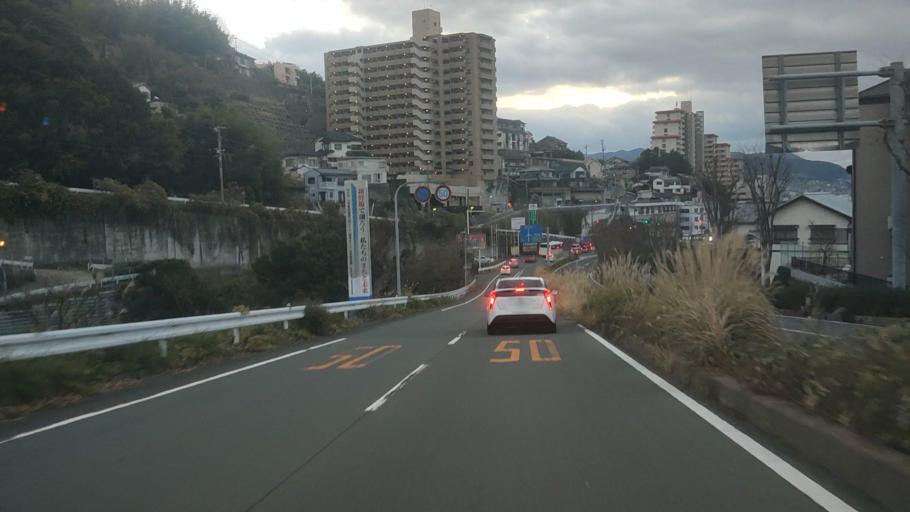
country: JP
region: Nagasaki
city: Nagasaki-shi
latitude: 32.7688
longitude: 129.8912
